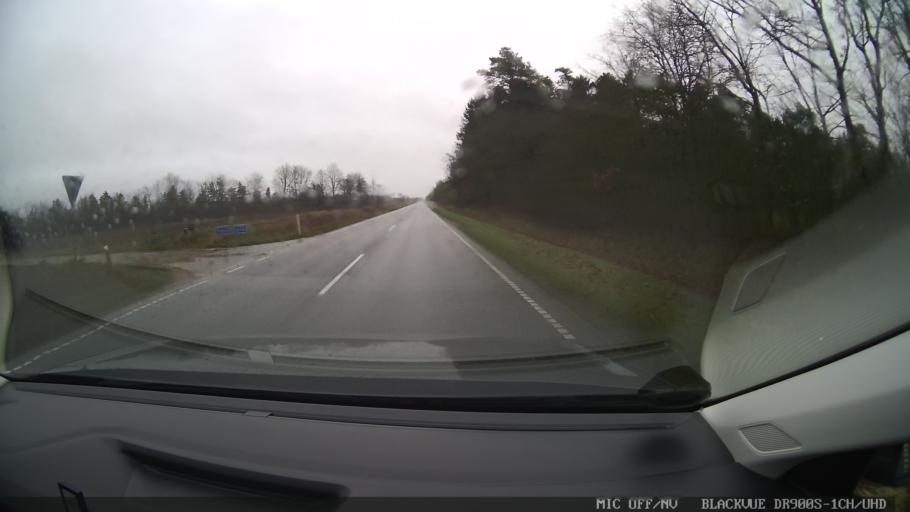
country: DK
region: Central Jutland
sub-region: Herning Kommune
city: Sunds
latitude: 56.2893
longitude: 8.9192
